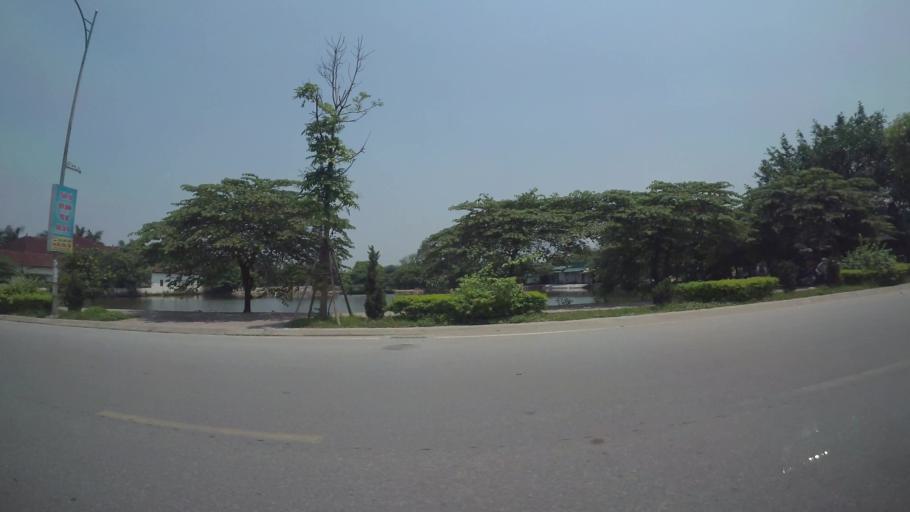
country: VN
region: Ha Noi
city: Trau Quy
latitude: 21.0276
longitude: 105.9114
